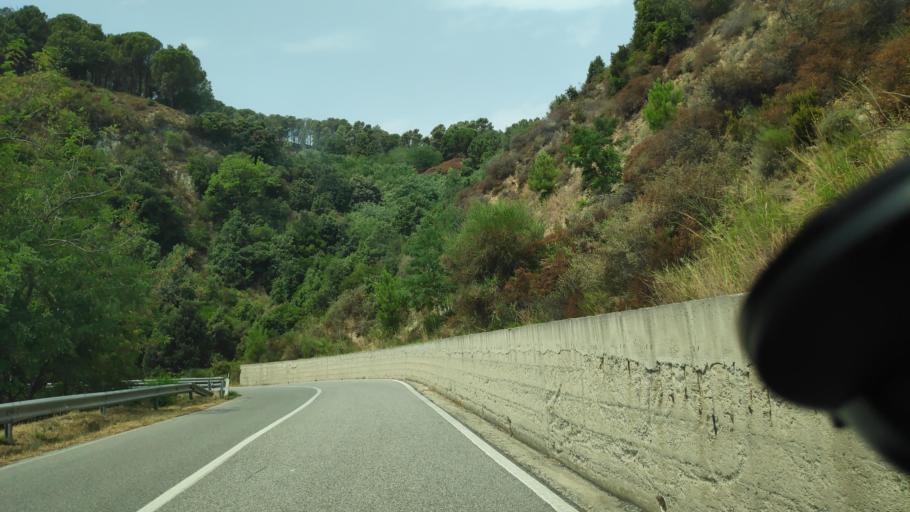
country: IT
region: Calabria
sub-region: Provincia di Catanzaro
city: San Sostene
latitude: 38.6402
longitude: 16.5087
